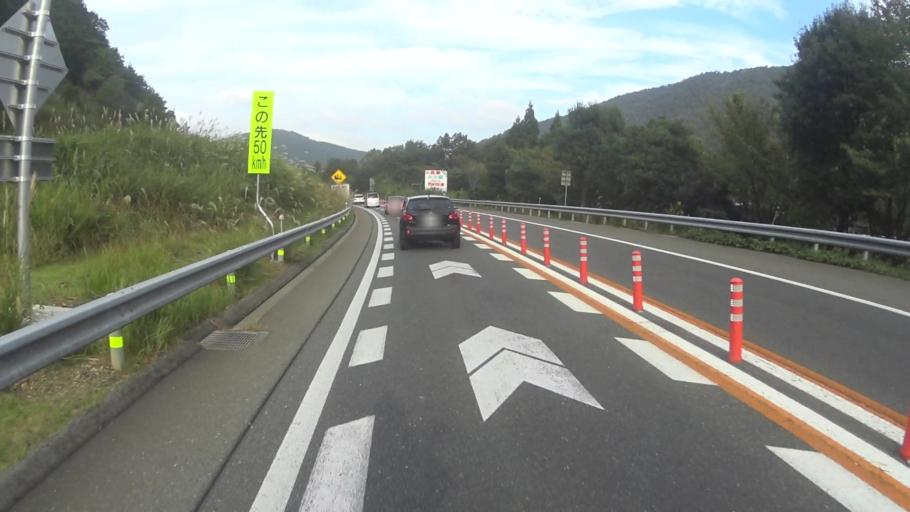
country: JP
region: Kyoto
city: Kameoka
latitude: 35.1436
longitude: 135.4426
